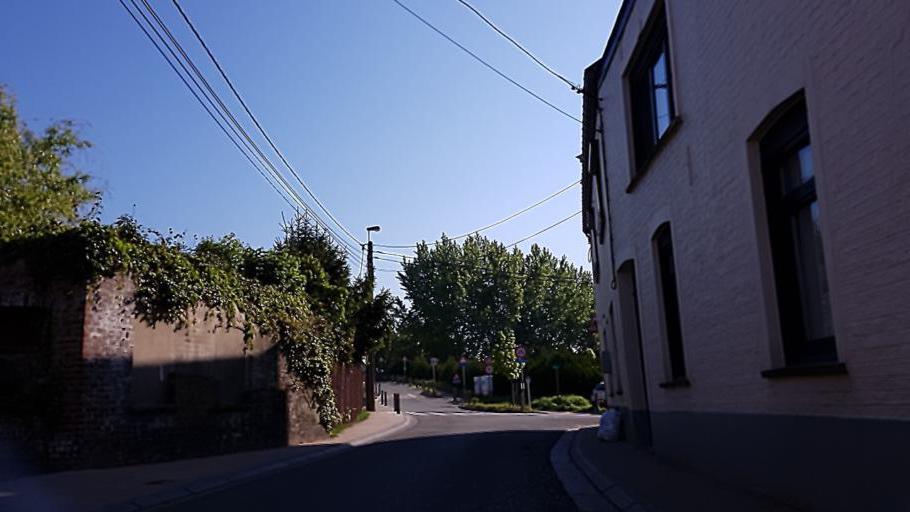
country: BE
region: Wallonia
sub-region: Province du Brabant Wallon
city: Wavre
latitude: 50.7251
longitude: 4.6156
